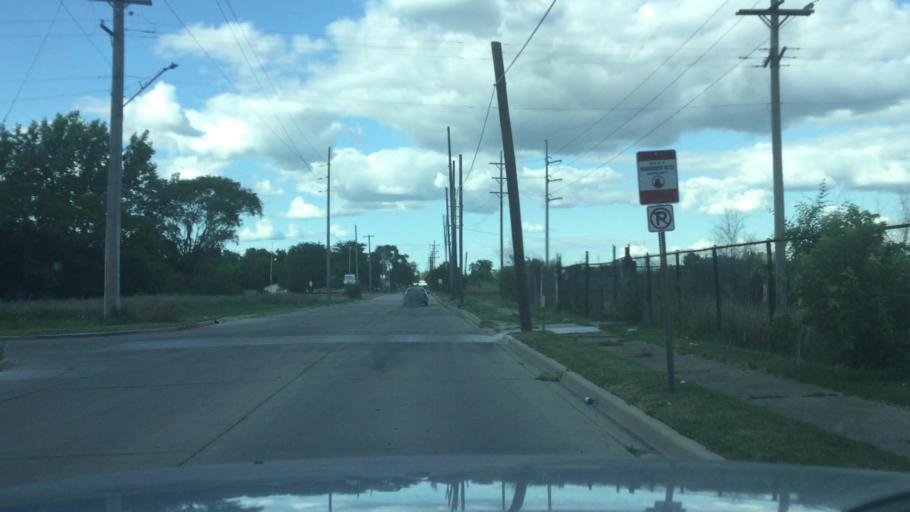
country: US
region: Michigan
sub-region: Saginaw County
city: Saginaw
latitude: 43.4020
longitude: -83.9773
